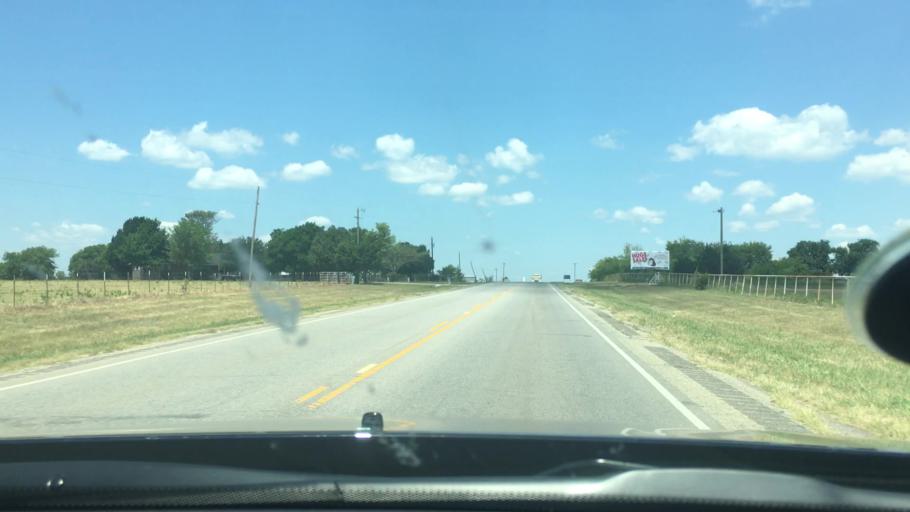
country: US
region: Oklahoma
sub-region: Marshall County
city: Oakland
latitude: 34.1261
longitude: -96.7864
